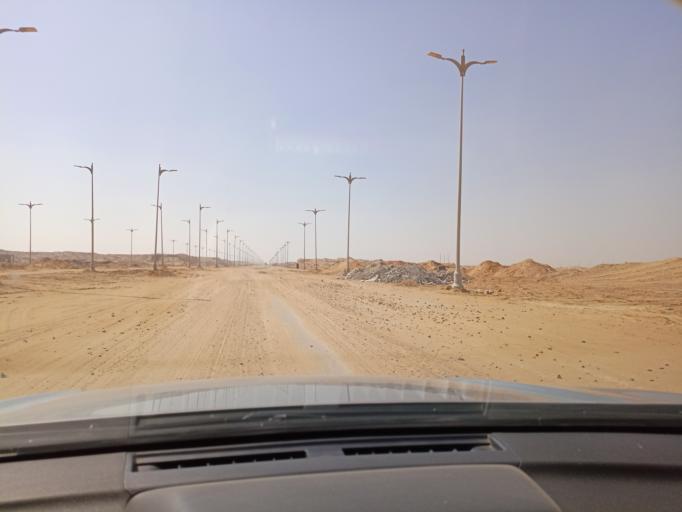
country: EG
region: Muhafazat al Qalyubiyah
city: Al Khankah
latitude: 30.0078
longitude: 31.6296
